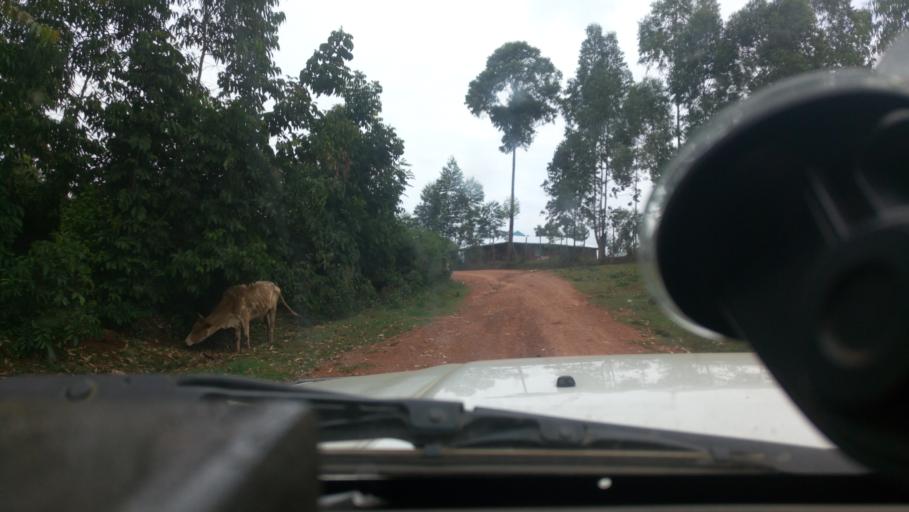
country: KE
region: Nyamira District
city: Nyamira
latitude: -0.4615
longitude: 34.9749
